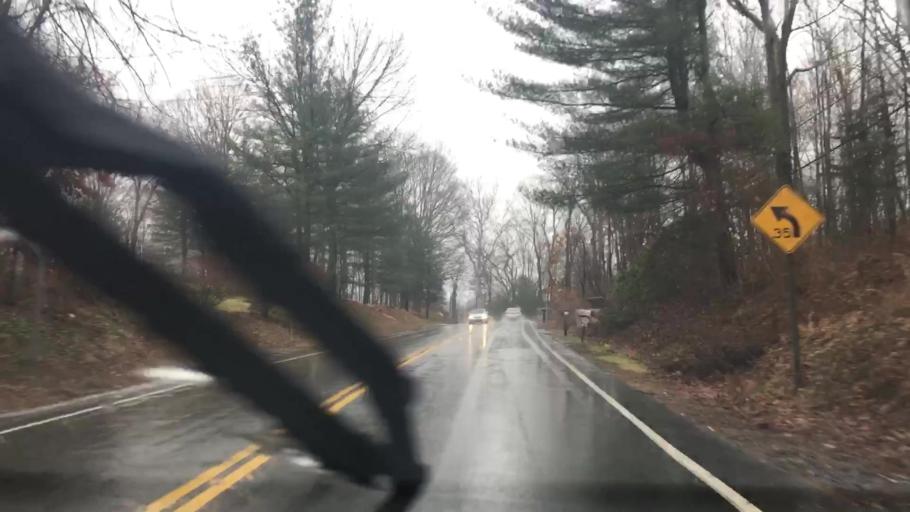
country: US
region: New York
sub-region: Putnam County
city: Putnam Lake
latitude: 41.4594
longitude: -73.5561
